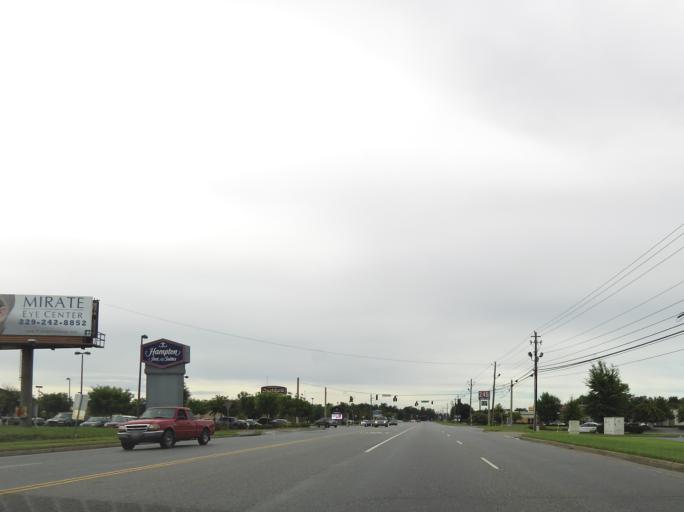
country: US
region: Georgia
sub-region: Lowndes County
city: Remerton
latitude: 30.8242
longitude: -83.3159
